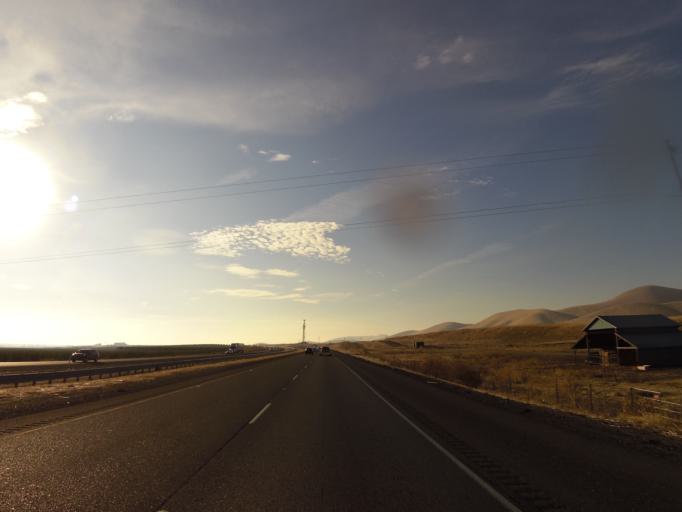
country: US
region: California
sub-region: Merced County
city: Gustine
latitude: 37.2028
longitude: -121.0782
